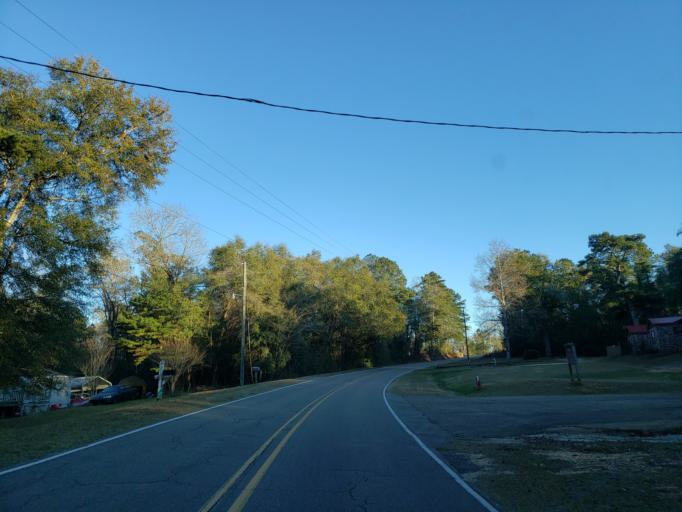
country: US
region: Mississippi
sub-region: Forrest County
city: Rawls Springs
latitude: 31.4274
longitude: -89.3550
